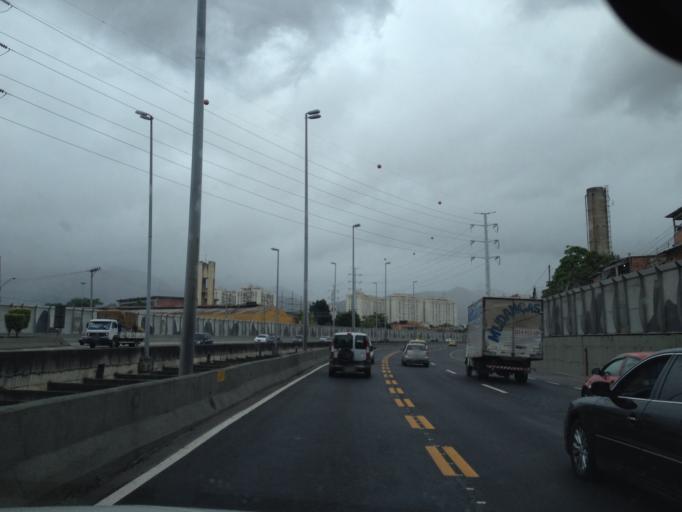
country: BR
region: Rio de Janeiro
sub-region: Rio De Janeiro
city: Rio de Janeiro
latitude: -22.8780
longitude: -43.2773
